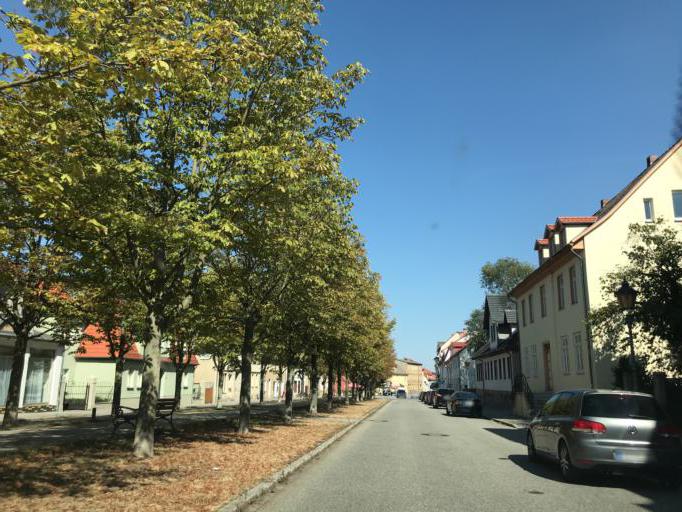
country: DE
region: Saxony-Anhalt
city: Ballenstedt
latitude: 51.7206
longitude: 11.2325
